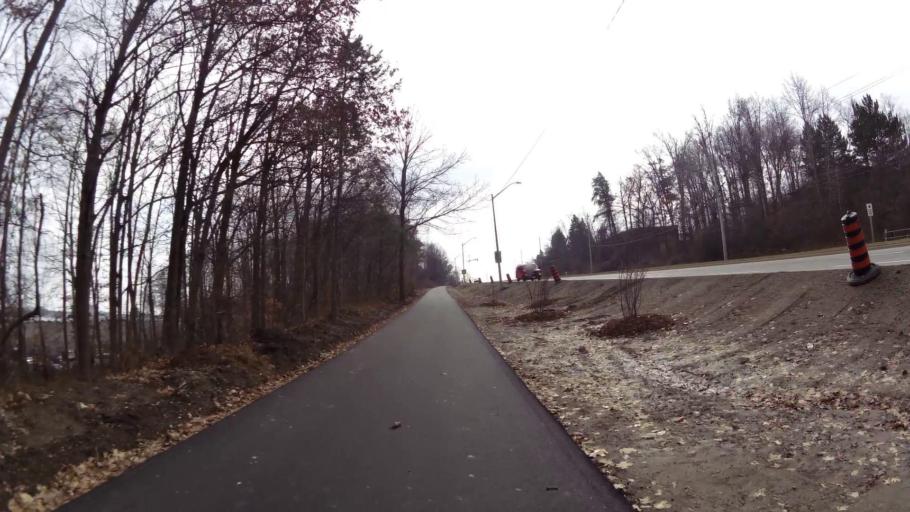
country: CA
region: Ontario
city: Kitchener
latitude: 43.4229
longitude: -80.4747
